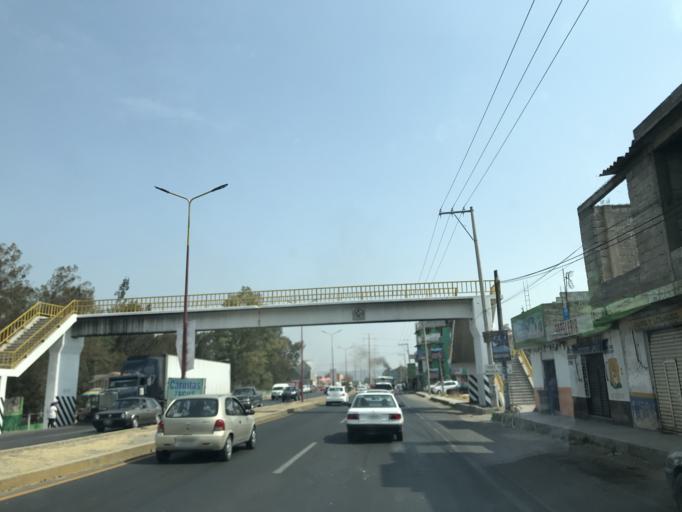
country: MX
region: Tlaxcala
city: La Magdalena Tlaltelulco
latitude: 19.2914
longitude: -98.1951
